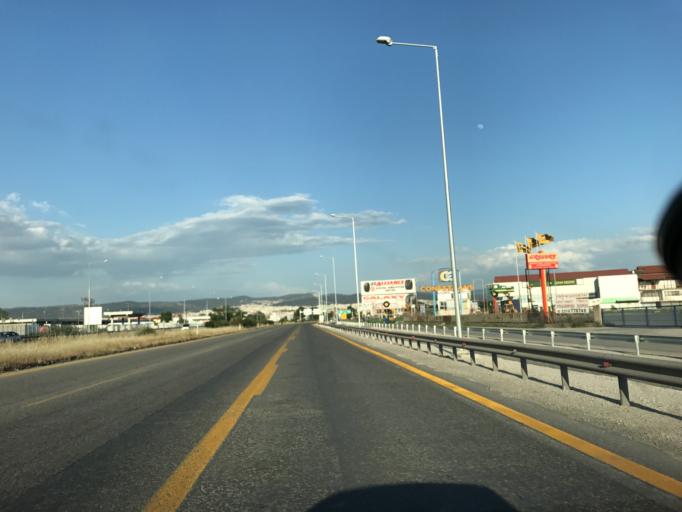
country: GR
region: Central Macedonia
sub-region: Nomos Thessalonikis
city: Menemeni
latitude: 40.6553
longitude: 22.8869
